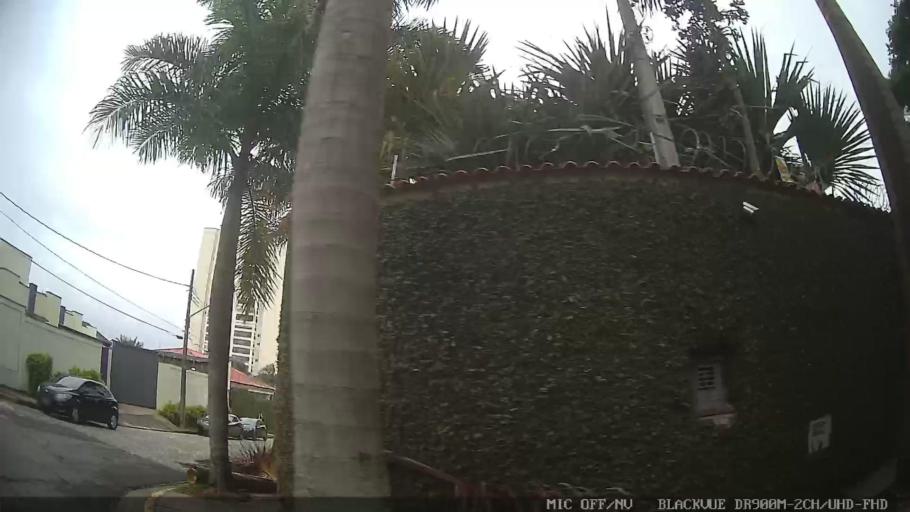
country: BR
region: Sao Paulo
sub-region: Mogi das Cruzes
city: Mogi das Cruzes
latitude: -23.5257
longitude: -46.1679
